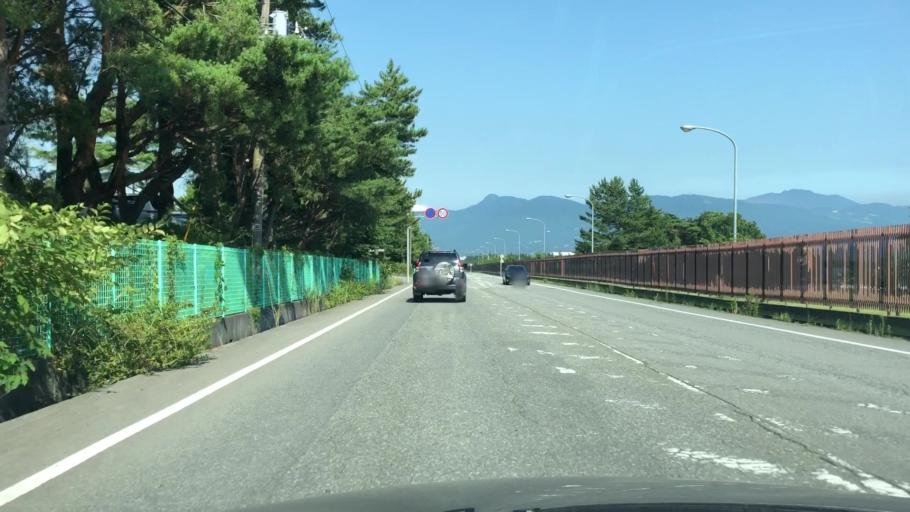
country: JP
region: Shizuoka
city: Gotemba
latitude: 35.3231
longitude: 138.8674
